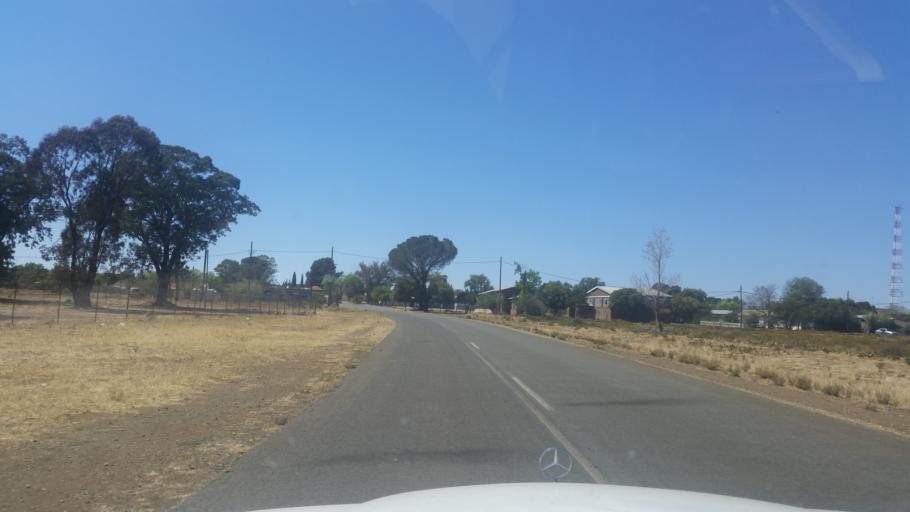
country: ZA
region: Eastern Cape
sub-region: Joe Gqabi District Municipality
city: Burgersdorp
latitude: -30.7742
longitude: 25.7954
